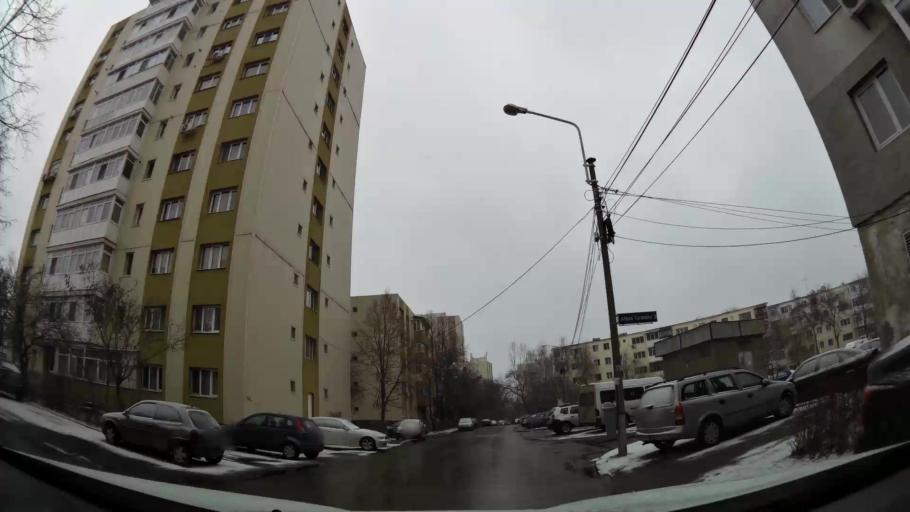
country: RO
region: Prahova
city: Ploiesti
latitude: 44.9461
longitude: 25.9949
